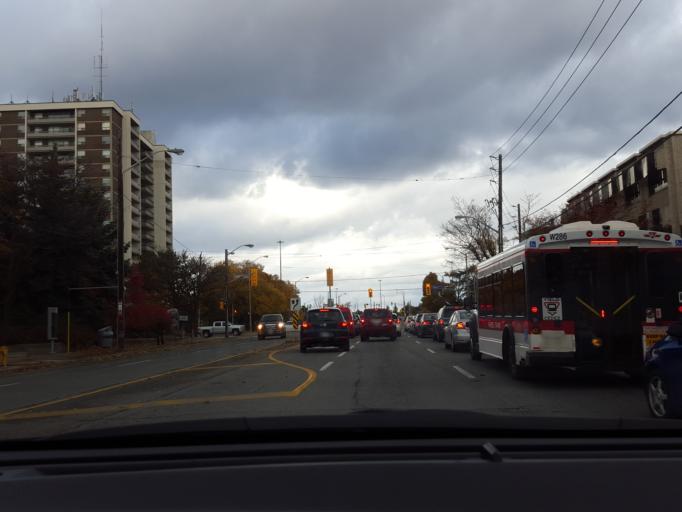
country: CA
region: Ontario
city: North York
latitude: 43.7392
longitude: -79.4213
